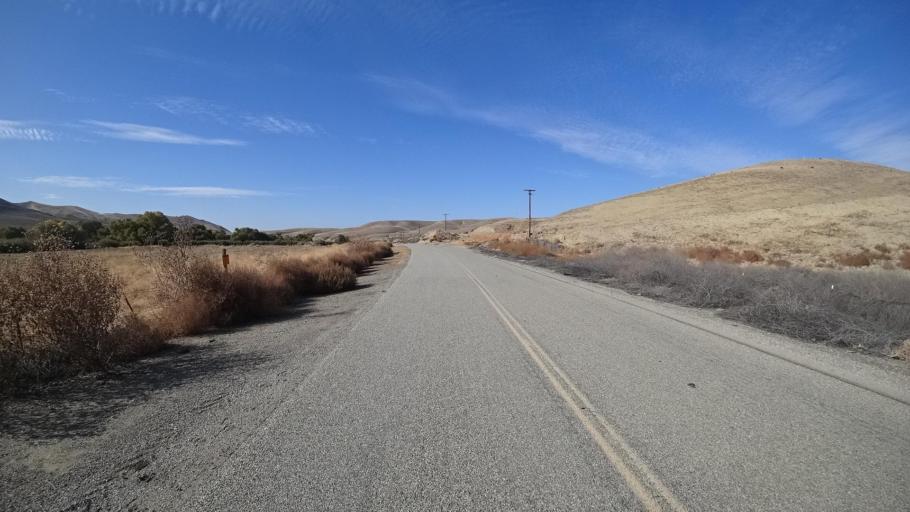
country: US
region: California
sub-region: Kern County
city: Oildale
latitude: 35.5247
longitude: -118.9328
